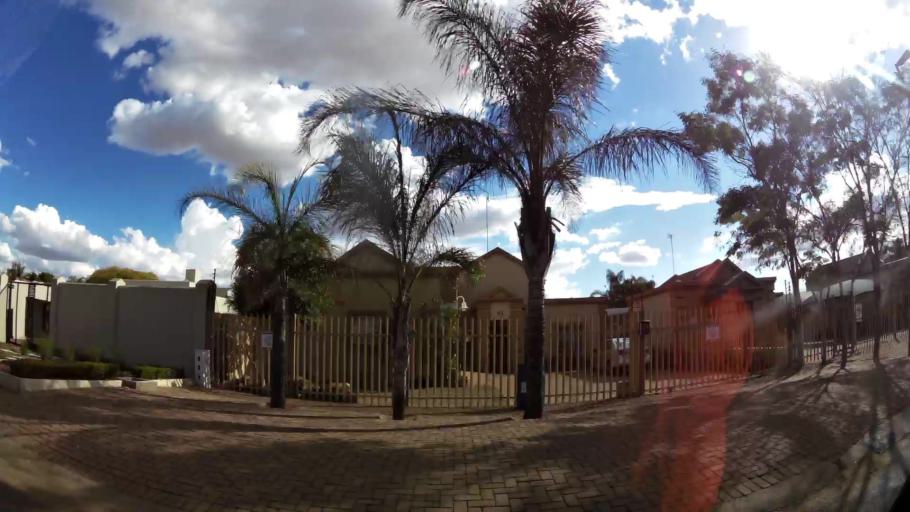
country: ZA
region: Limpopo
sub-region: Capricorn District Municipality
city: Polokwane
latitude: -23.8994
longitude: 29.4753
